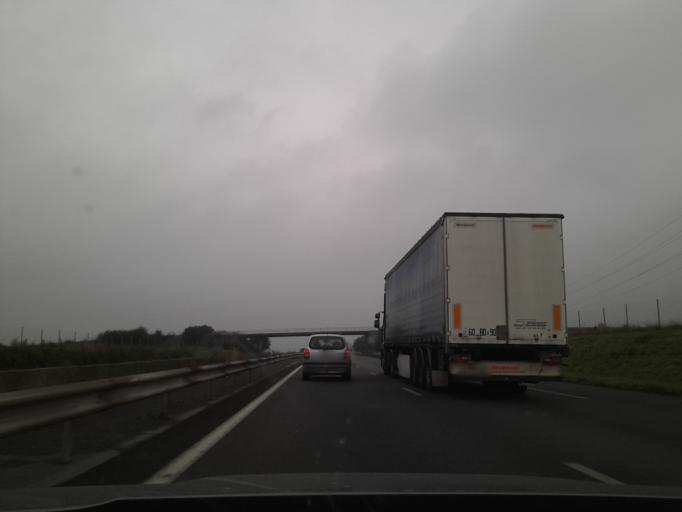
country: FR
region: Nord-Pas-de-Calais
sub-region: Departement du Nord
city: Iwuy
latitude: 50.2363
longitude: 3.2879
